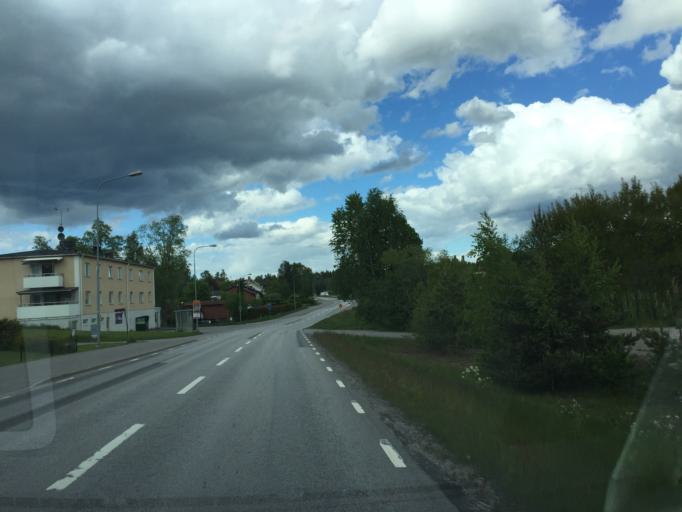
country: SE
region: OEstergoetland
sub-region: Finspangs Kommun
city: Finspang
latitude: 58.6826
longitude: 15.7505
